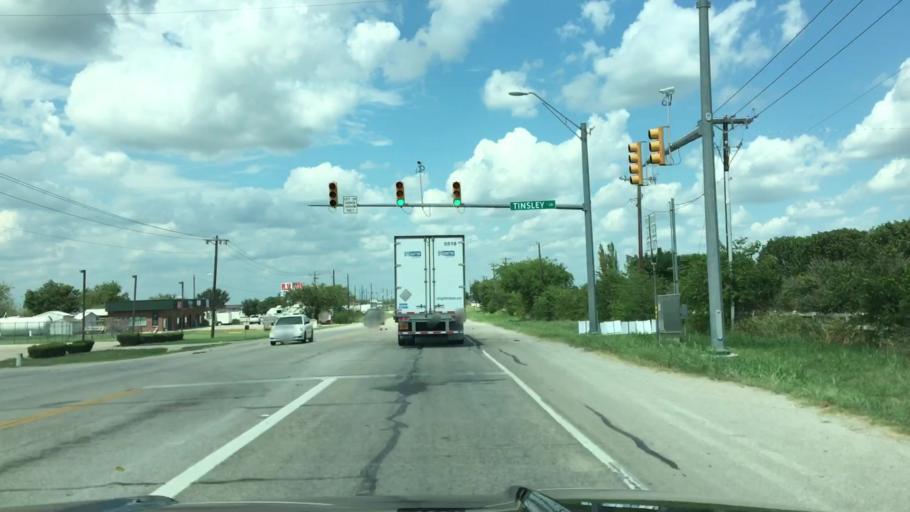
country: US
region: Texas
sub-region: Tarrant County
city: Pecan Acres
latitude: 32.9531
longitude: -97.4208
